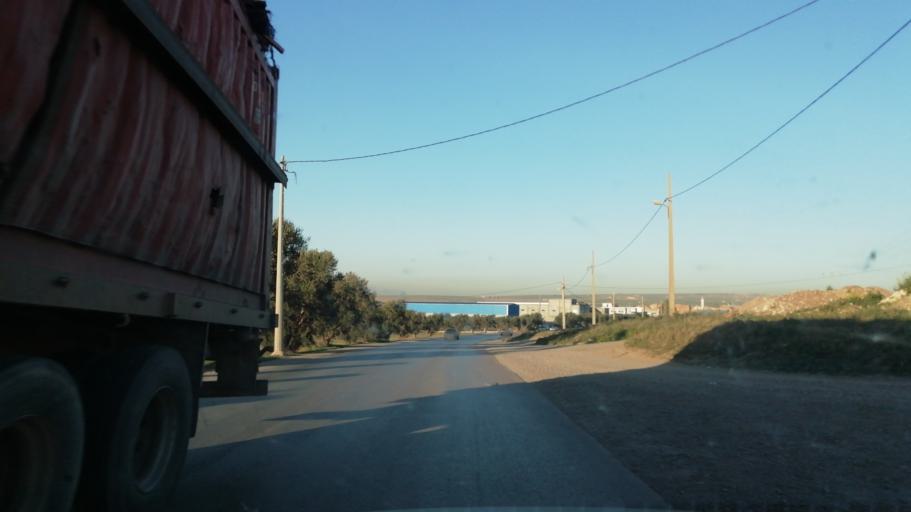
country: DZ
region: Oran
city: Es Senia
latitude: 35.5553
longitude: -0.5720
